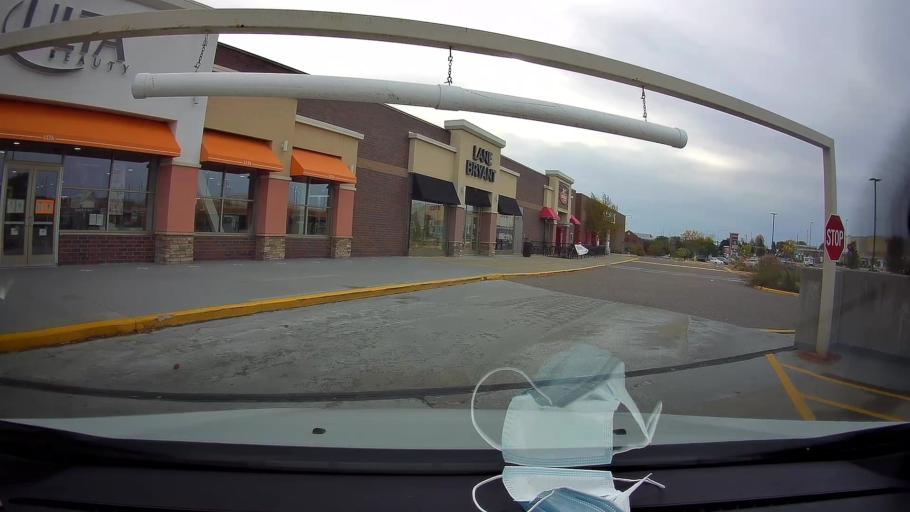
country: US
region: Minnesota
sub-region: Ramsey County
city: Roseville
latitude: 45.0162
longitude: -93.1709
